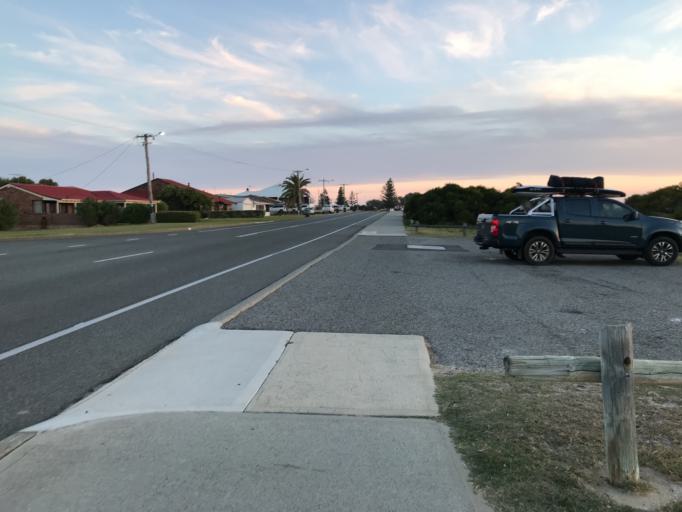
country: AU
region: Western Australia
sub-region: Rockingham
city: Shoalwater
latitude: -32.3018
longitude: 115.7035
